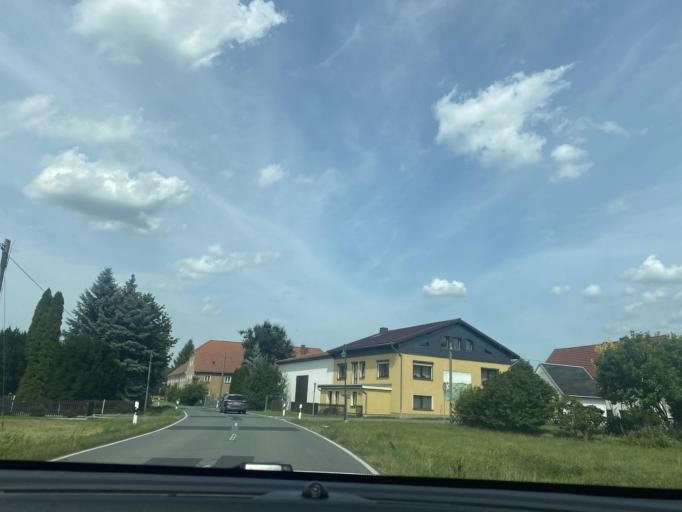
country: DE
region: Saxony
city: Grosshennersdorf
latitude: 50.9975
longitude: 14.7939
